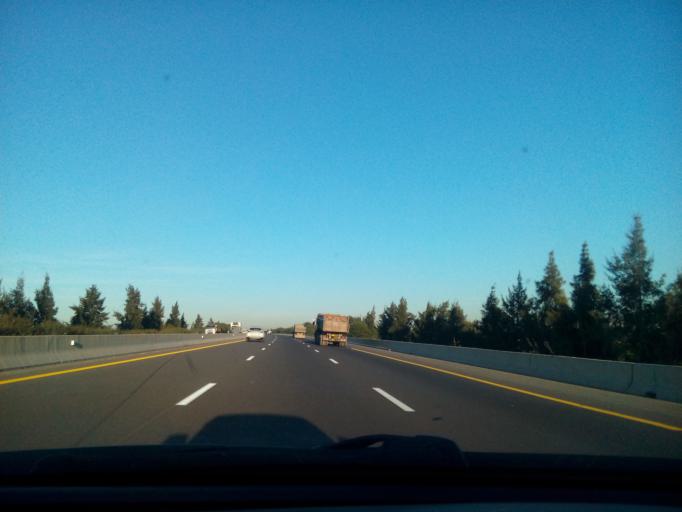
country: DZ
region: Relizane
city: Oued Rhiou
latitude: 35.9614
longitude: 0.8884
